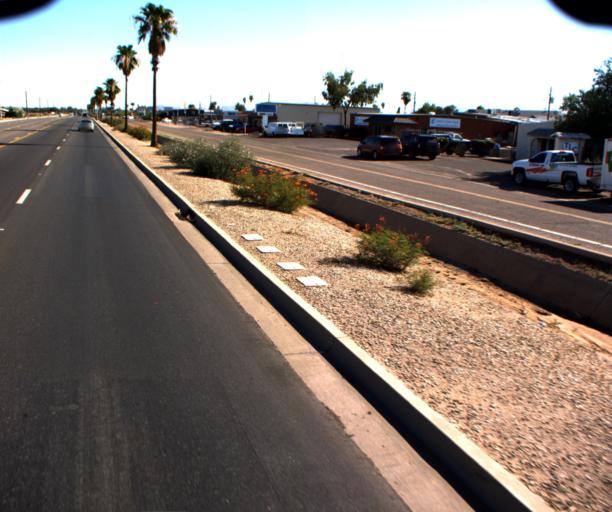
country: US
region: Arizona
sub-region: Pinal County
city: Casa Grande
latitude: 32.8996
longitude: -111.7572
